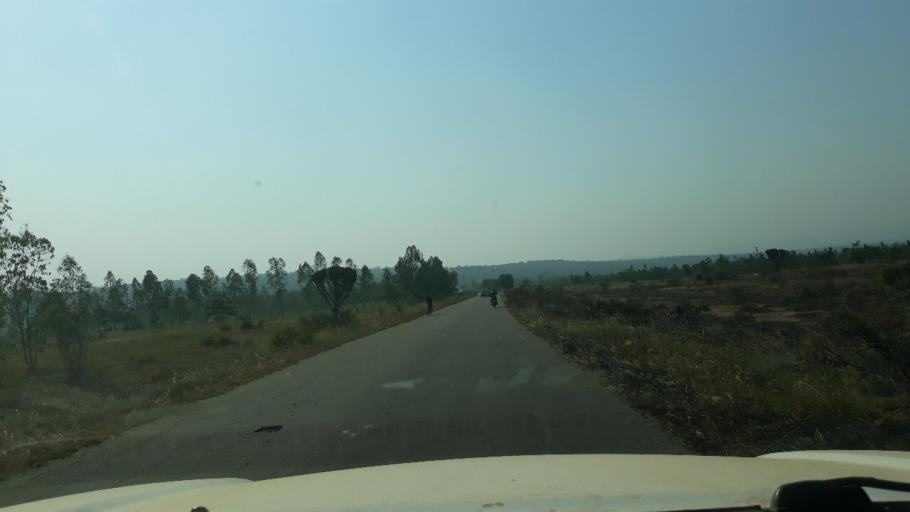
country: BI
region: Cibitoke
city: Cibitoke
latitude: -2.9268
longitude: 29.0619
